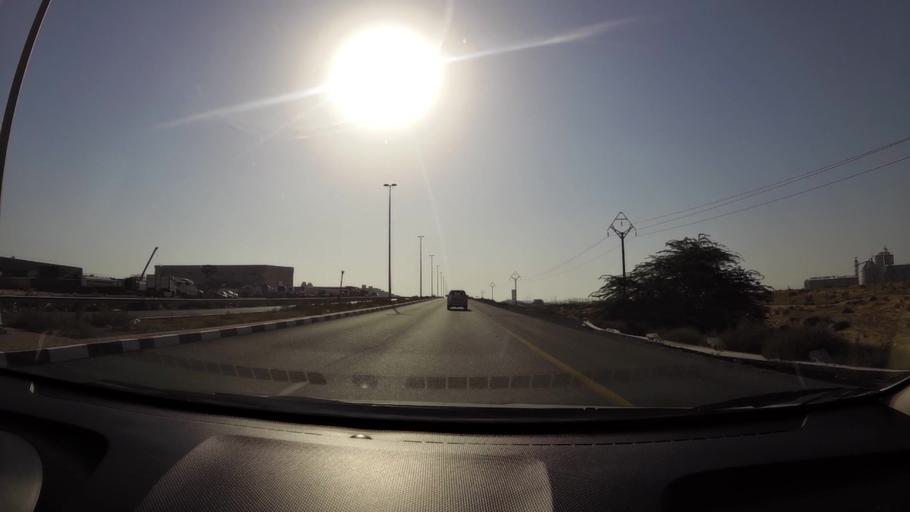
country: AE
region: Umm al Qaywayn
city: Umm al Qaywayn
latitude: 25.4385
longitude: 55.5586
